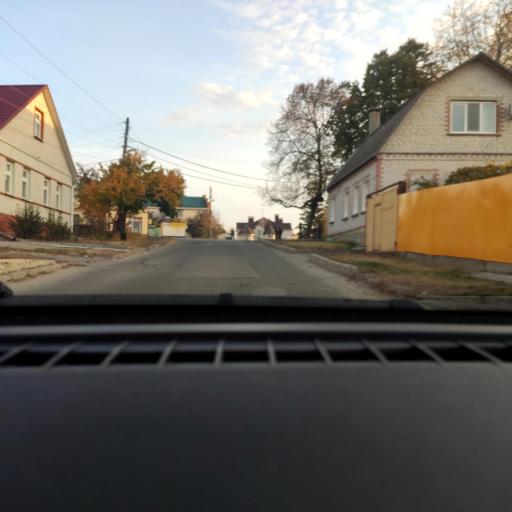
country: RU
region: Voronezj
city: Voronezh
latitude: 51.6286
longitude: 39.1931
